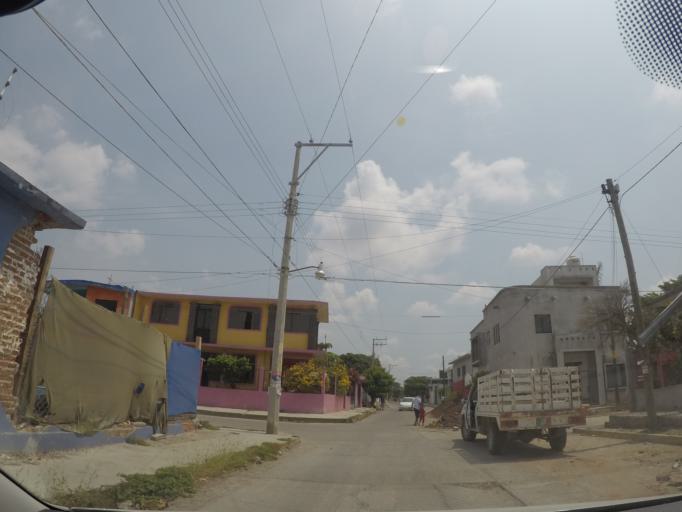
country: MX
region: Oaxaca
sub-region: El Espinal
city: El Espinal
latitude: 16.4825
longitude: -95.0407
